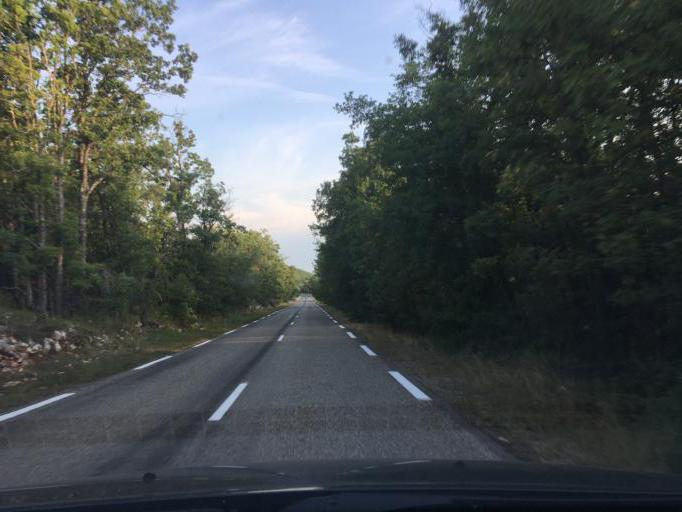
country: FR
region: Provence-Alpes-Cote d'Azur
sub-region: Departement du Var
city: Aups
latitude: 43.7241
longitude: 6.2229
